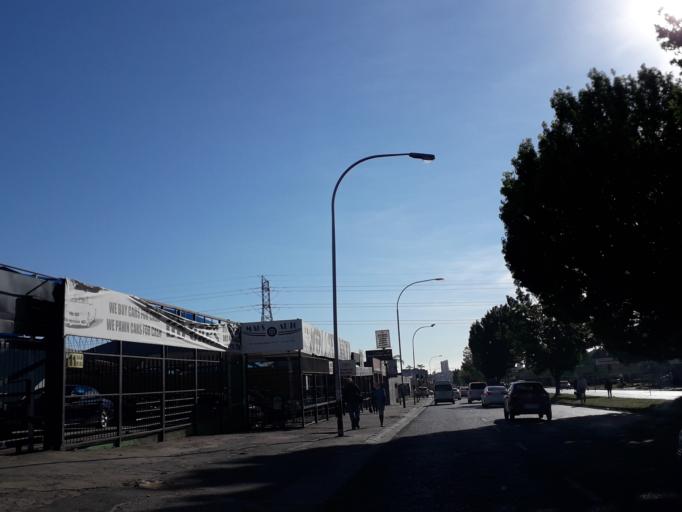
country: ZA
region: Gauteng
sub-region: City of Johannesburg Metropolitan Municipality
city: Roodepoort
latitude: -26.1744
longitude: 27.9543
